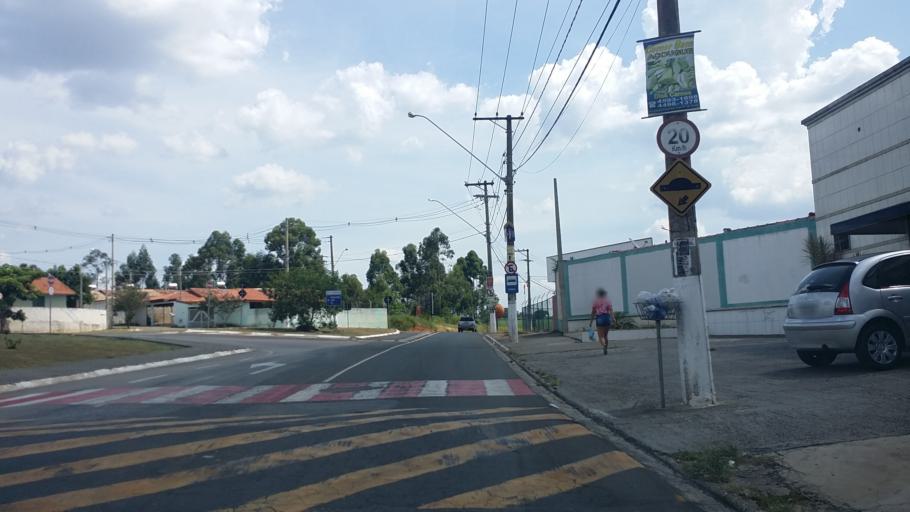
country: BR
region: Sao Paulo
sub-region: Itupeva
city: Itupeva
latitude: -23.1750
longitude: -47.0529
